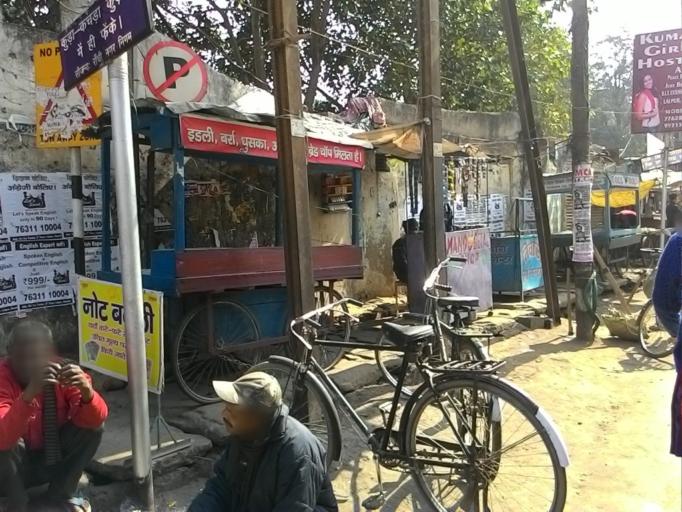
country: IN
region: Jharkhand
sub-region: Ranchi
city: Ranchi
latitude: 23.3718
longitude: 85.3384
